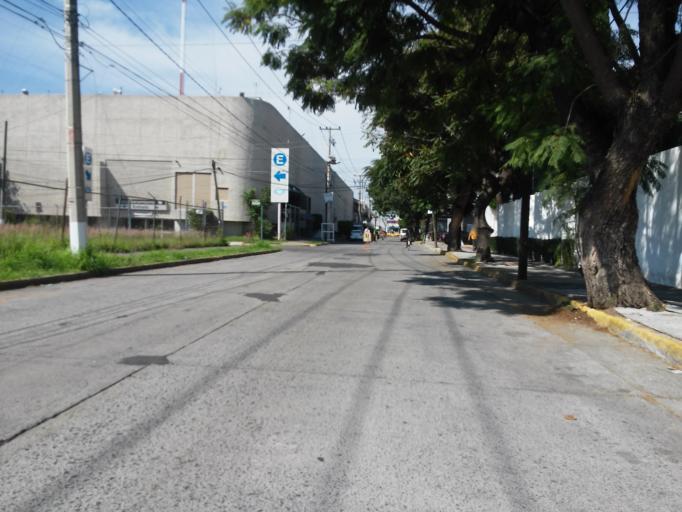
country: MX
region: Jalisco
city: Guadalajara
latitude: 20.6573
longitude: -103.3963
